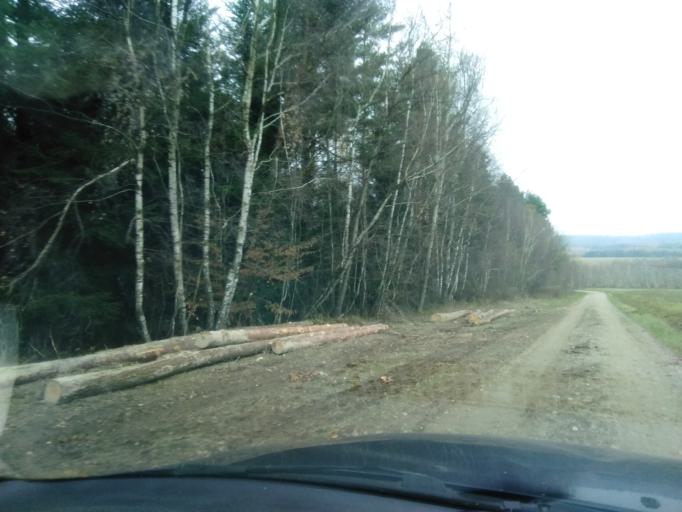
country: PL
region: Subcarpathian Voivodeship
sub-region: Powiat strzyzowski
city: Wysoka Strzyzowska
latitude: 49.7959
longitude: 21.7800
